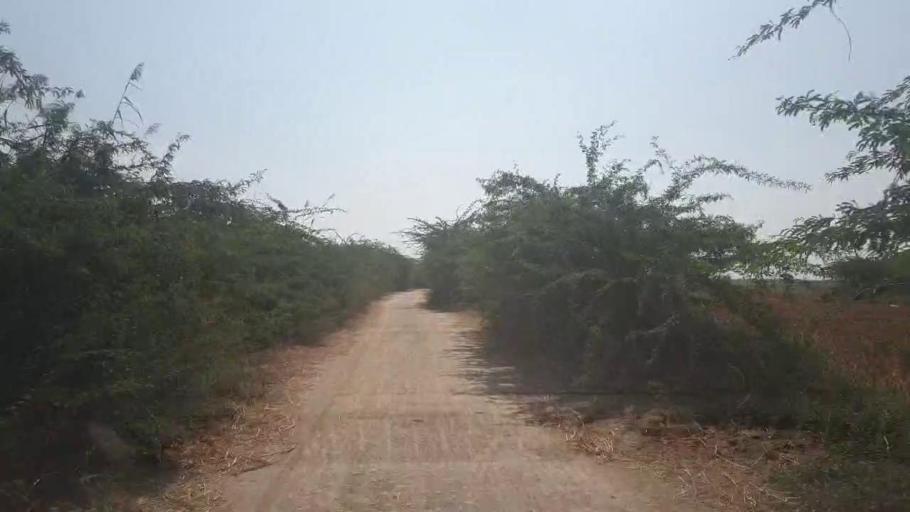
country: PK
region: Sindh
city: Badin
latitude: 24.6446
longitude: 68.9122
